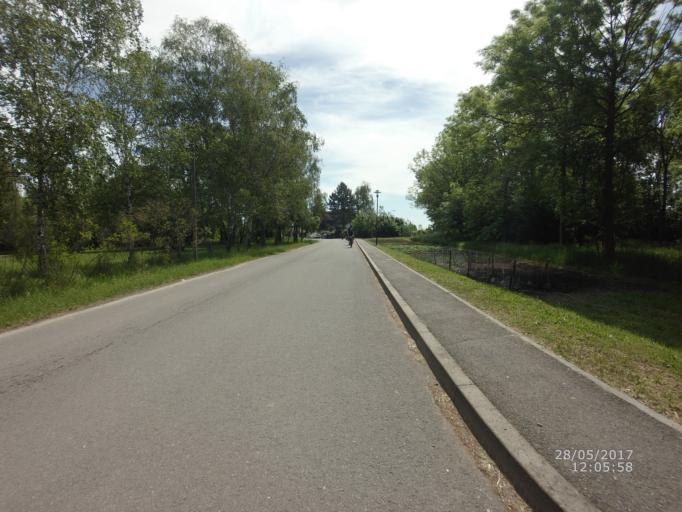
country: DE
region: Thuringia
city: Buchel
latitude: 51.2472
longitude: 11.1593
